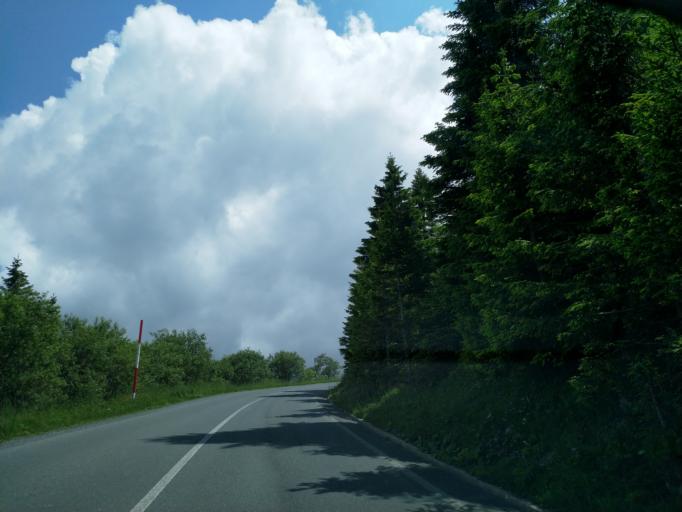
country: XK
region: Mitrovica
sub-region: Komuna e Leposaviqit
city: Leposaviq
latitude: 43.3205
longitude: 20.8387
